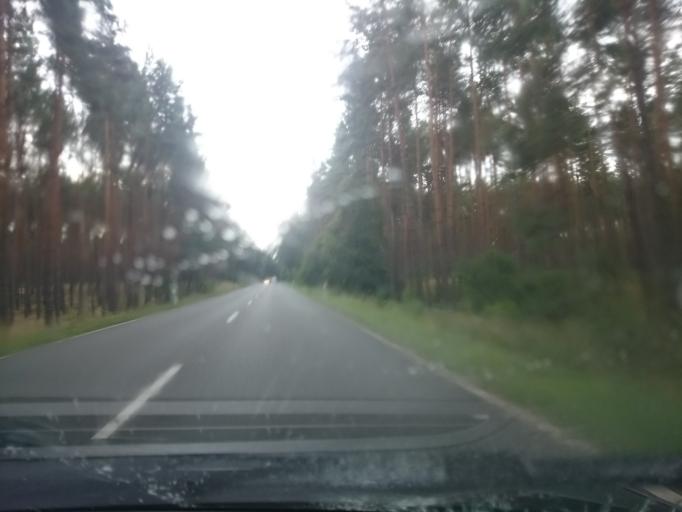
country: DE
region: Brandenburg
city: Furstenberg
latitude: 53.2244
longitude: 13.1210
